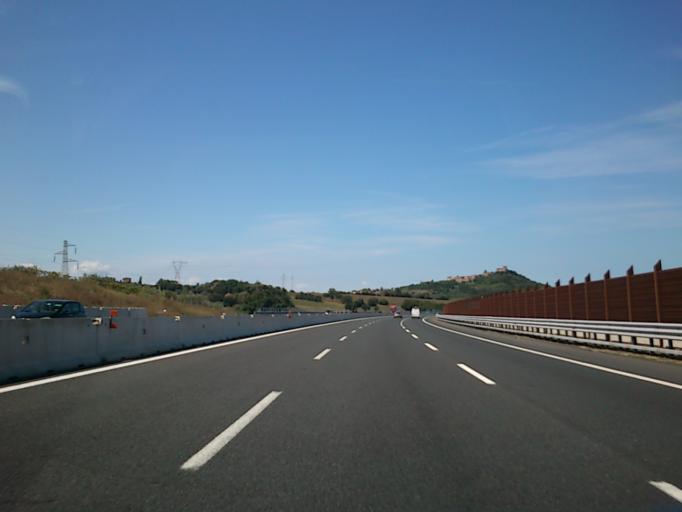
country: IT
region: The Marches
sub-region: Provincia di Pesaro e Urbino
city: Gradara
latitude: 43.9284
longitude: 12.7954
